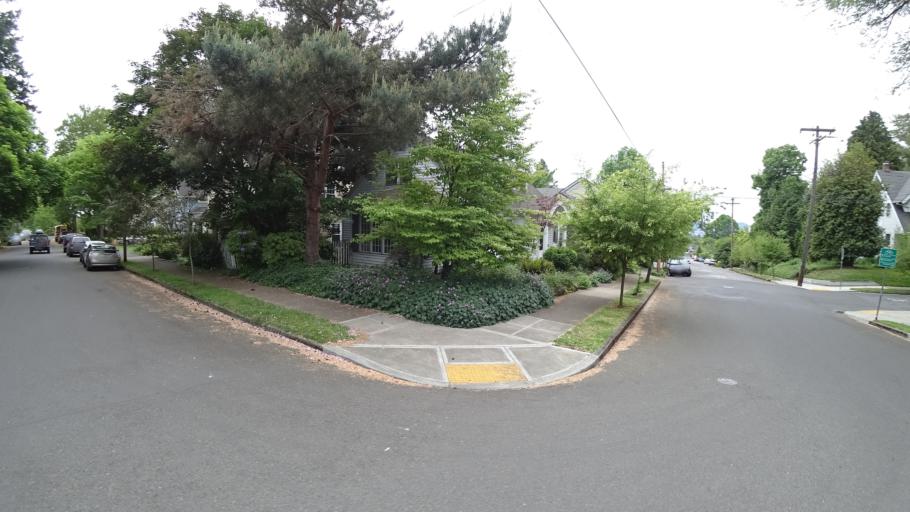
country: US
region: Oregon
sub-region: Multnomah County
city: Lents
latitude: 45.5154
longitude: -122.6085
